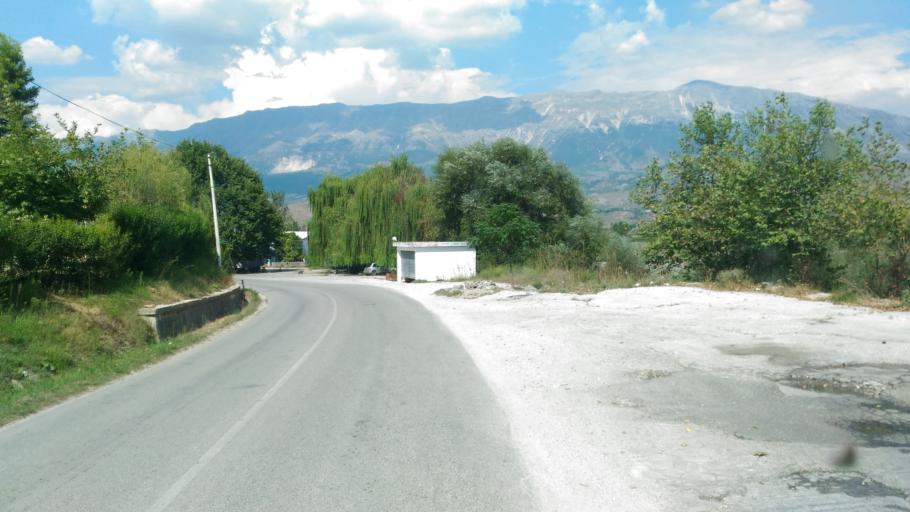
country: AL
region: Gjirokaster
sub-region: Rrethi i Gjirokastres
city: Dervician
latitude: 40.0604
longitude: 20.1725
